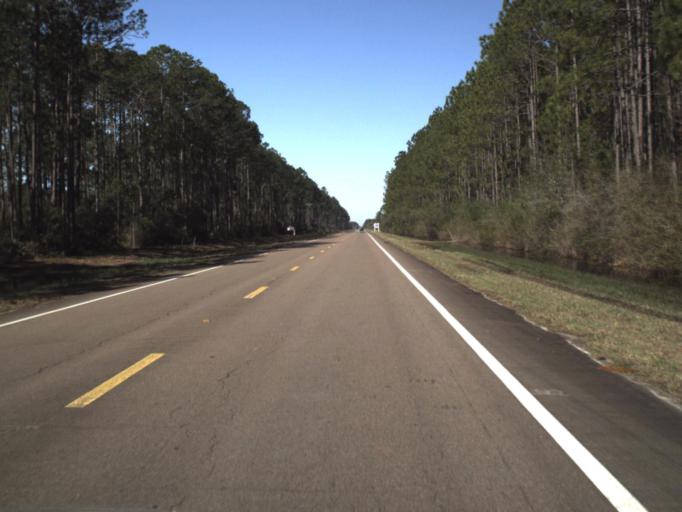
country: US
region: Florida
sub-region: Bay County
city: Callaway
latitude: 30.1380
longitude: -85.3858
